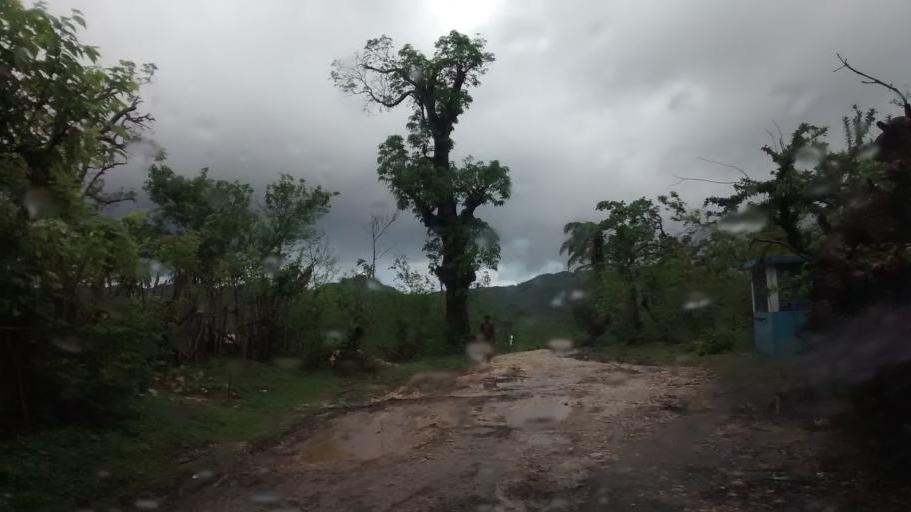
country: HT
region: Grandans
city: Corail
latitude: 18.5356
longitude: -73.9923
